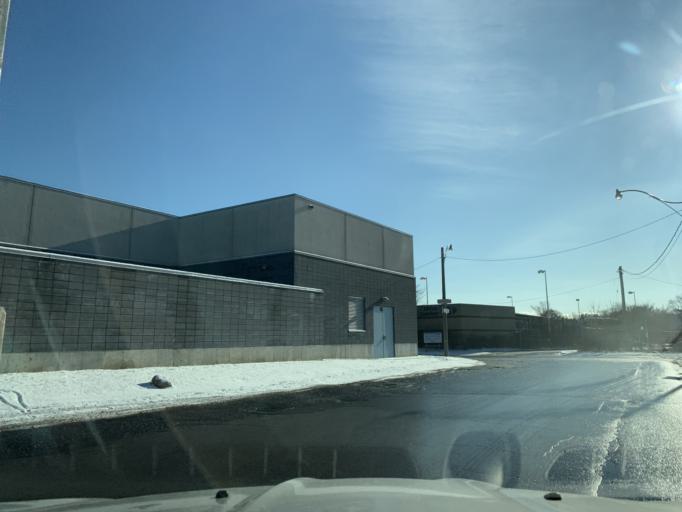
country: CA
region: Ontario
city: Toronto
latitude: 43.6692
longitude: -79.4721
